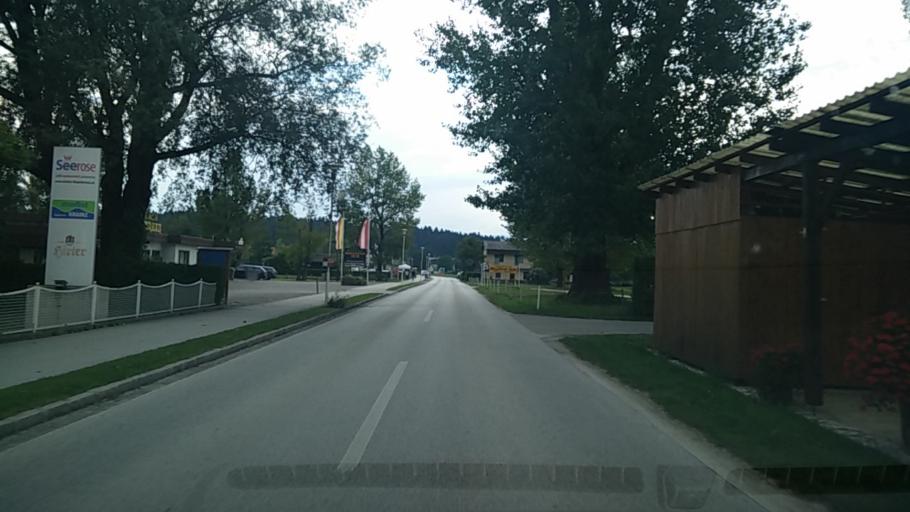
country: AT
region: Carinthia
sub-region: Politischer Bezirk Volkermarkt
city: Eberndorf
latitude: 46.6060
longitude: 14.5972
